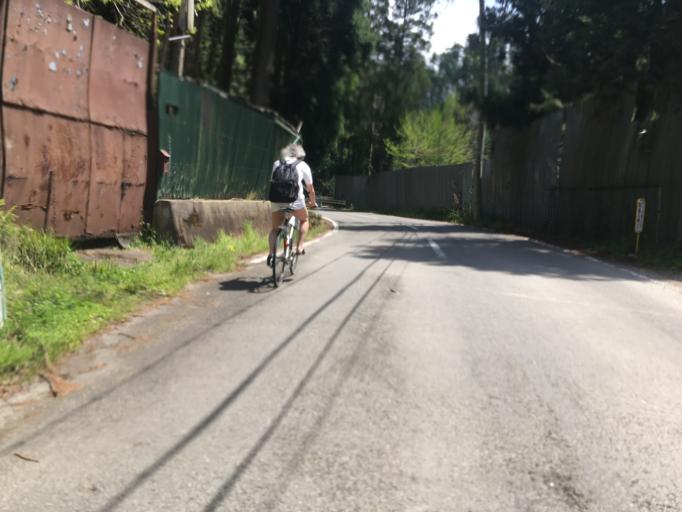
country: JP
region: Kyoto
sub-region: Kyoto-shi
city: Kamigyo-ku
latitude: 35.1071
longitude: 135.7376
